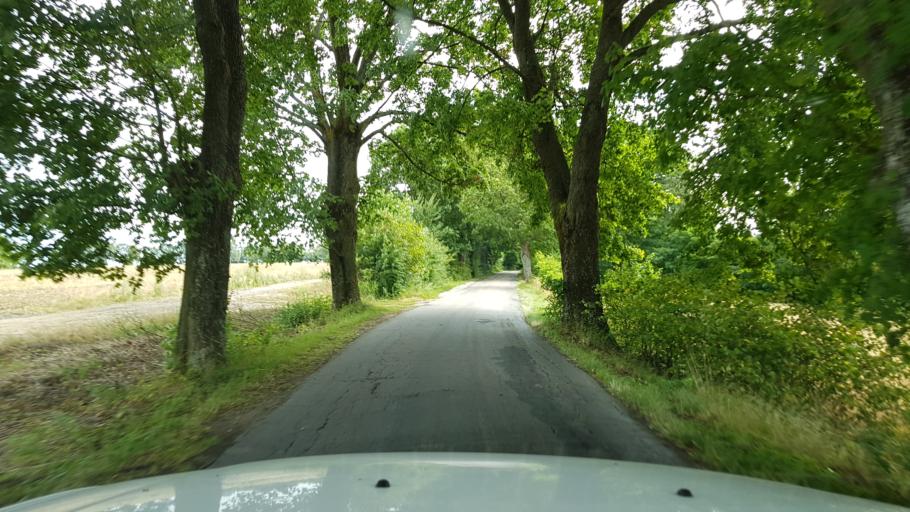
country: PL
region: West Pomeranian Voivodeship
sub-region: Powiat koszalinski
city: Mielno
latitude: 54.1598
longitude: 16.0731
